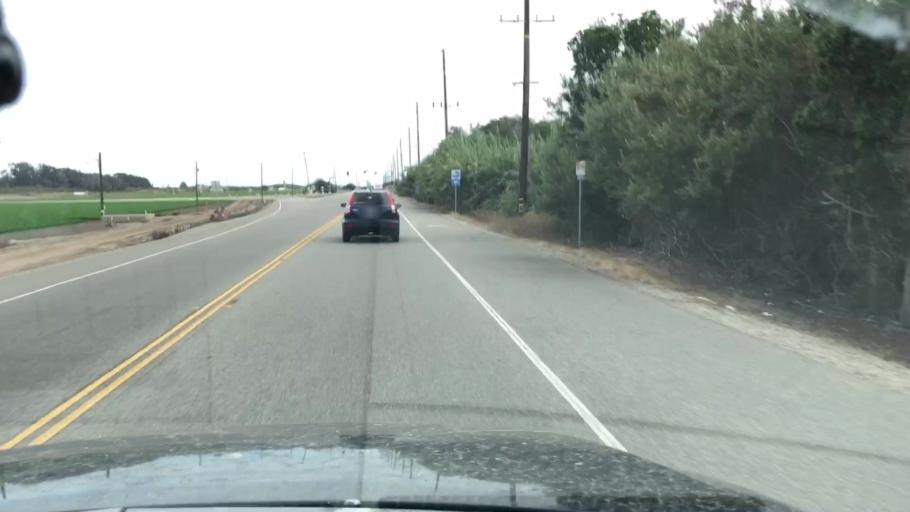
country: US
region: California
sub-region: Ventura County
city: Oxnard Shores
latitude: 34.2207
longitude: -119.2549
